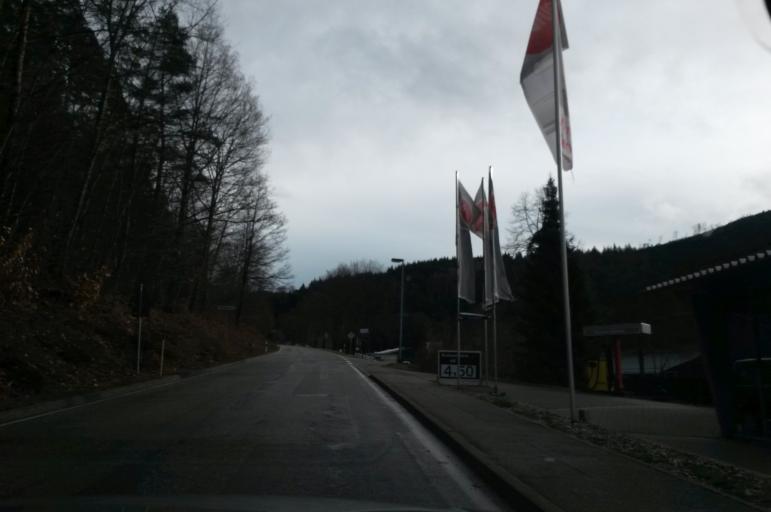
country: DE
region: Baden-Wuerttemberg
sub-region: Karlsruhe Region
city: Bad Herrenalb
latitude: 48.8063
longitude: 8.4490
